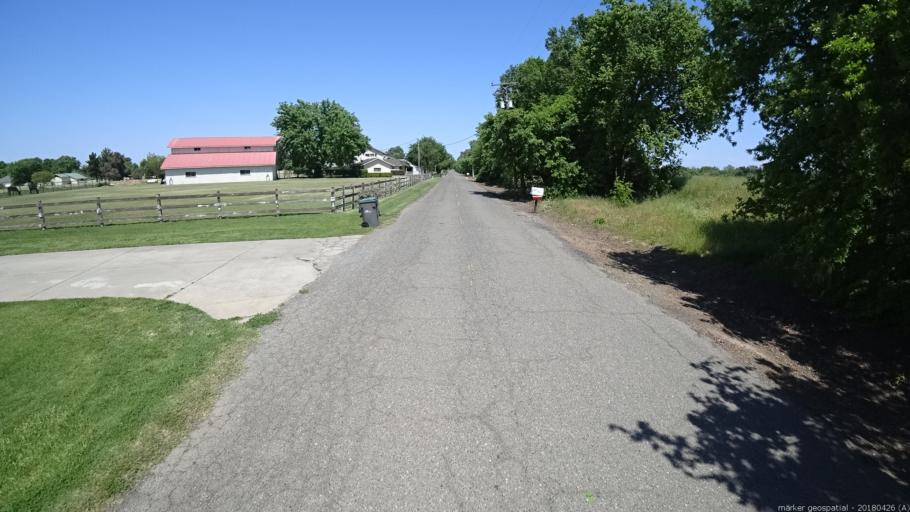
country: US
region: California
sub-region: Yolo County
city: West Sacramento
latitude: 38.5270
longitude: -121.5473
